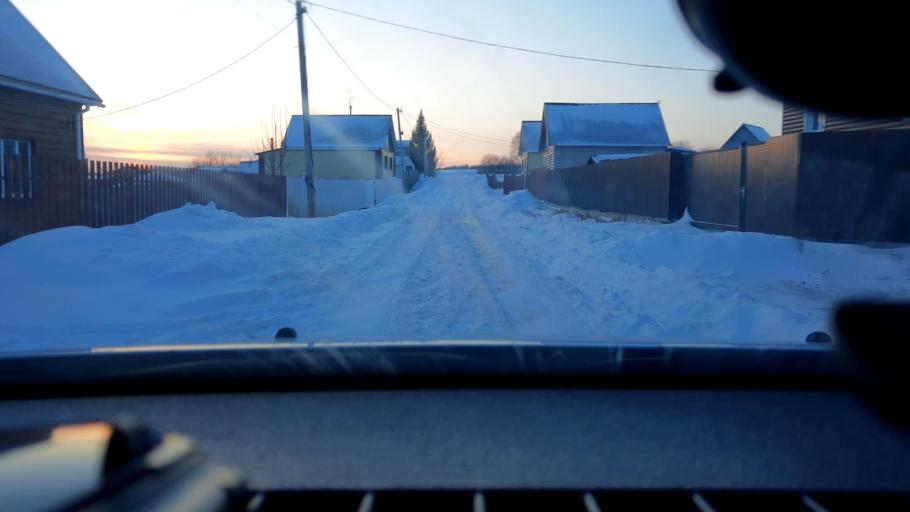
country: RU
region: Bashkortostan
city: Iglino
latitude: 54.8622
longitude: 56.4743
